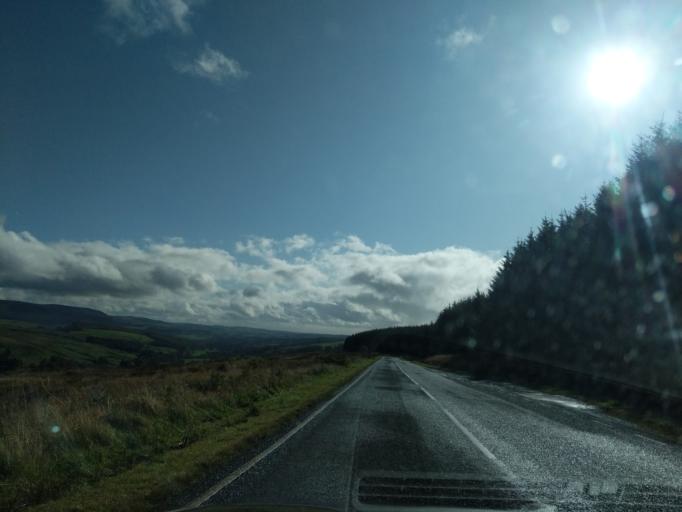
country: GB
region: Scotland
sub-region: Dumfries and Galloway
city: Moffat
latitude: 55.3754
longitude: -3.4770
